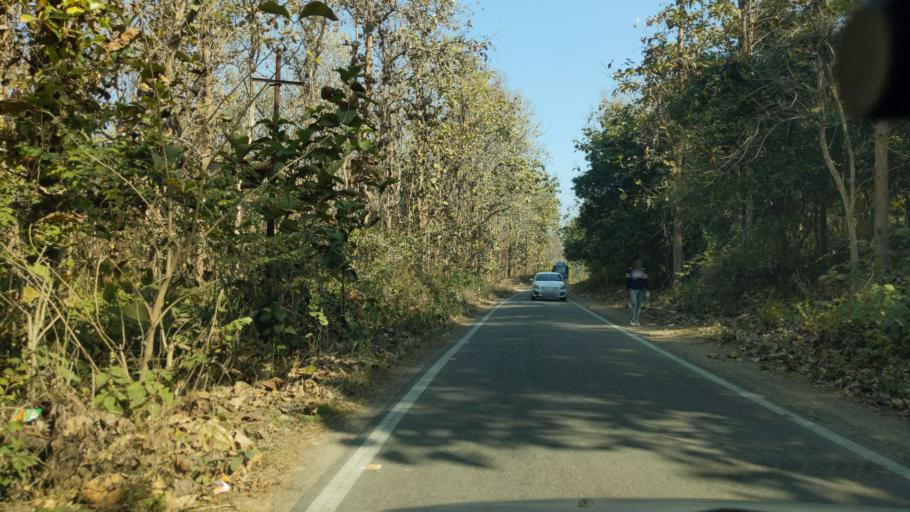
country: IN
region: Uttarakhand
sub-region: Naini Tal
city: Ramnagar
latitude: 29.4051
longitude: 79.1372
